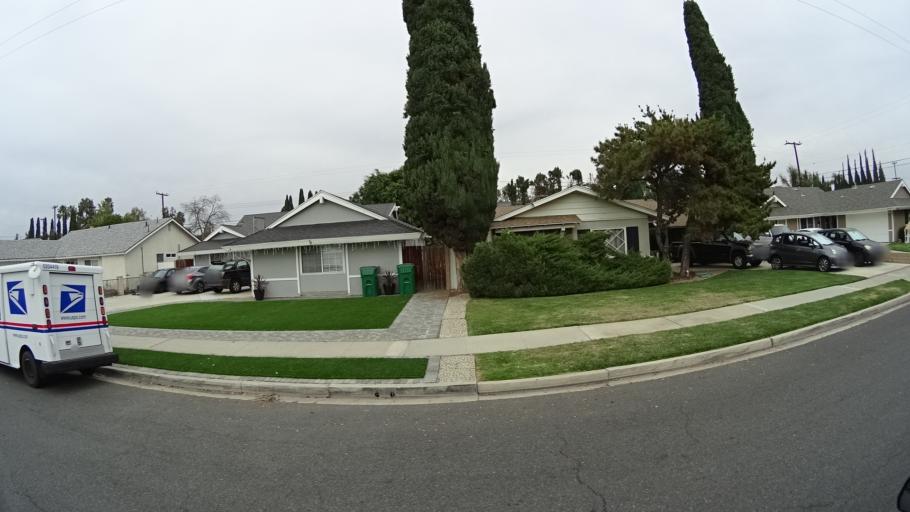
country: US
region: California
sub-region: Orange County
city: Tustin
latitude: 33.7415
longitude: -117.8039
